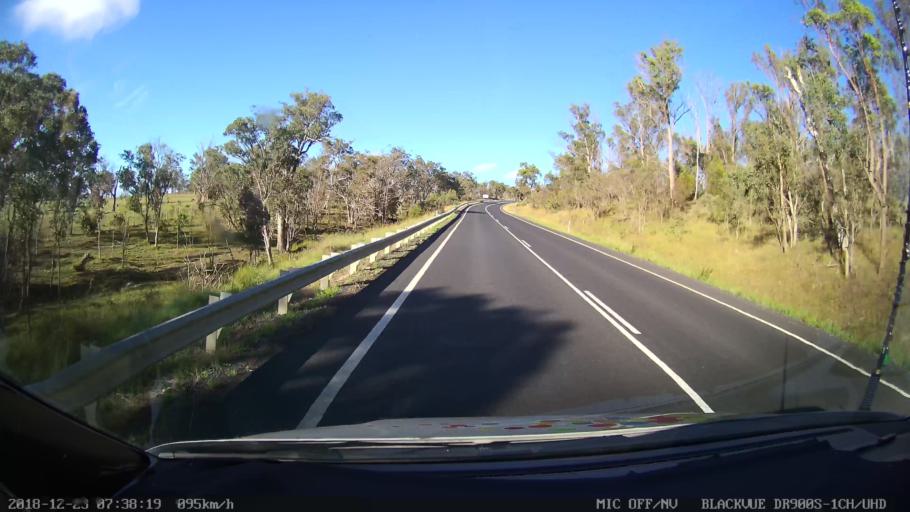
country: AU
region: New South Wales
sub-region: Armidale Dumaresq
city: Enmore
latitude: -30.5181
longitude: 152.0357
